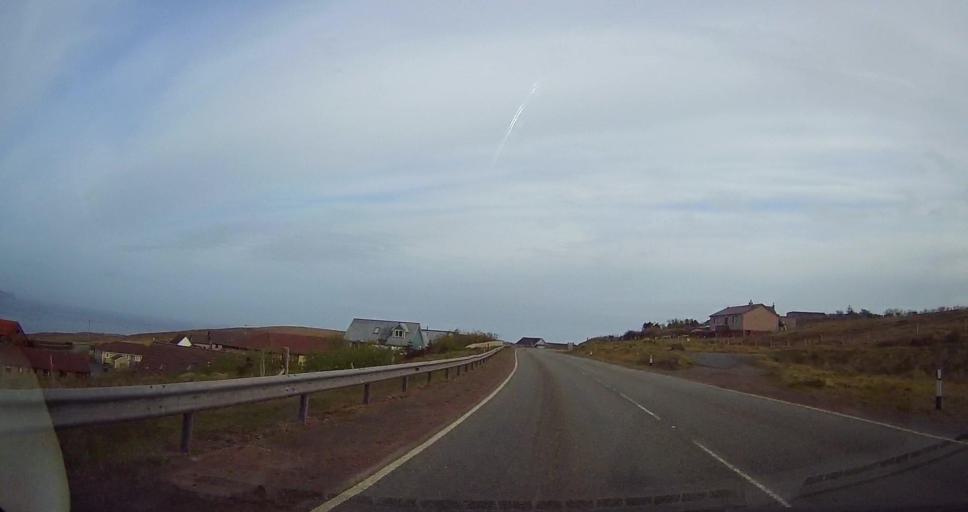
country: GB
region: Scotland
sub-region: Shetland Islands
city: Lerwick
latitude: 60.1236
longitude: -1.2170
